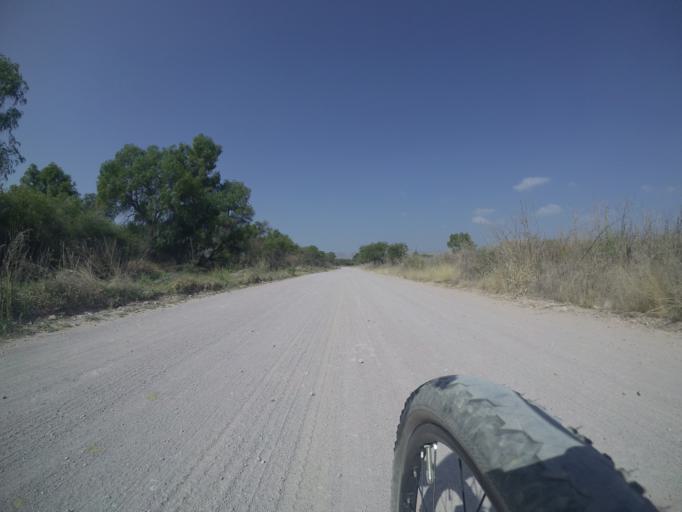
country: MX
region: Aguascalientes
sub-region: Jesus Maria
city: Paseos de las Haciendas [Fraccionamiento]
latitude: 21.9990
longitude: -102.3373
